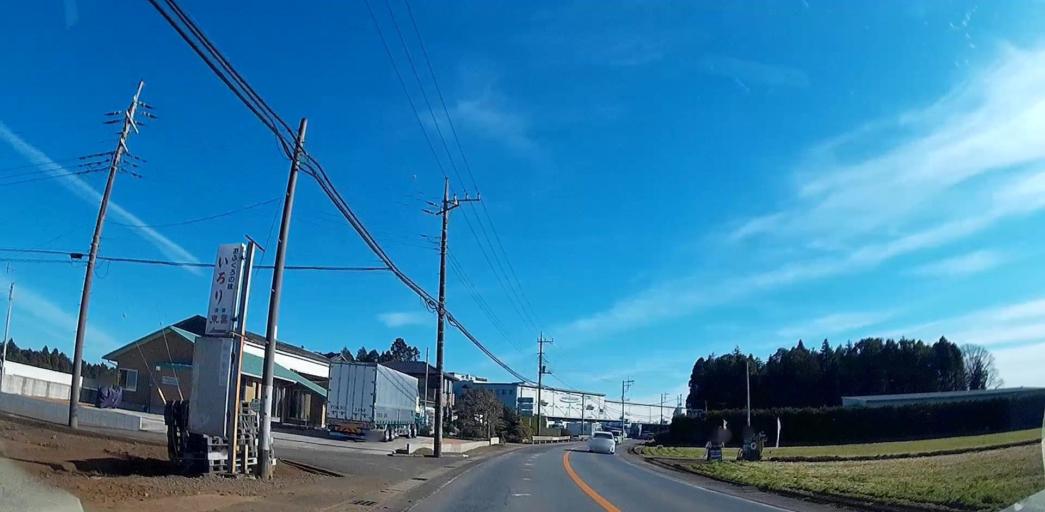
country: JP
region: Chiba
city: Narita
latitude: 35.7678
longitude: 140.4420
